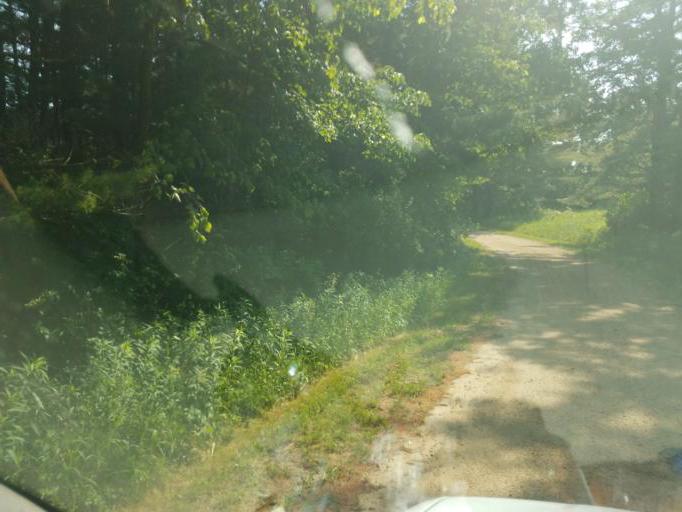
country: US
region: Wisconsin
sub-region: Monroe County
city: Cashton
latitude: 43.7029
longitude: -90.5685
